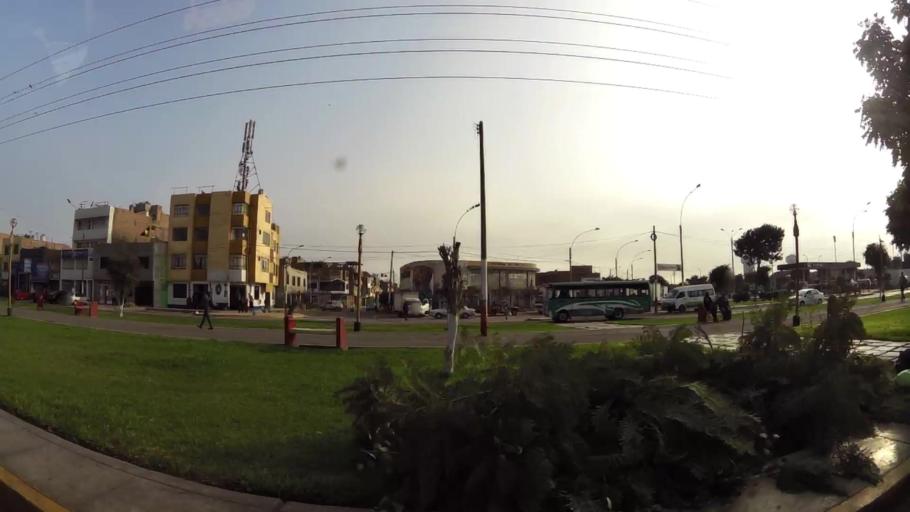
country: PE
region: Callao
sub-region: Callao
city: Callao
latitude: -12.0143
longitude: -77.0946
